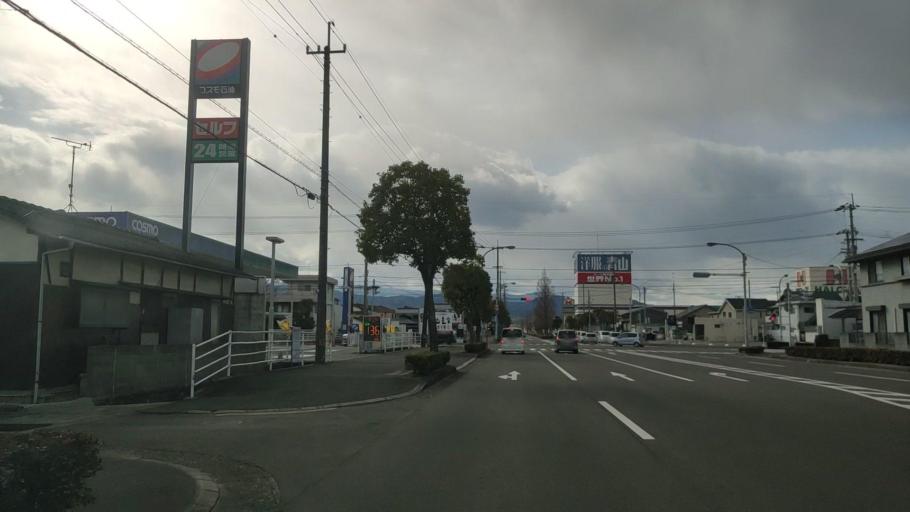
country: JP
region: Ehime
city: Saijo
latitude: 34.0489
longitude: 133.0098
